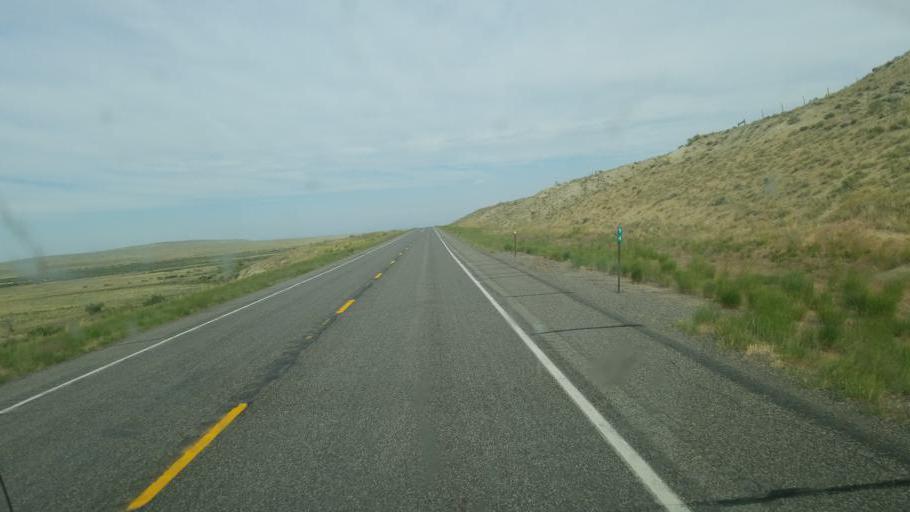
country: US
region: Wyoming
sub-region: Fremont County
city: Riverton
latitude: 43.2212
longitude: -107.9961
